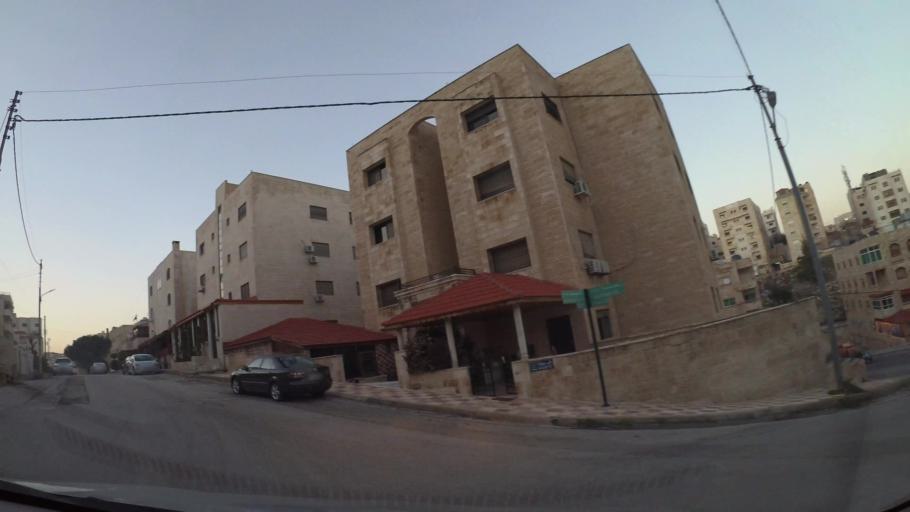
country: JO
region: Amman
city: Al Jubayhah
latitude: 31.9989
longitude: 35.8577
